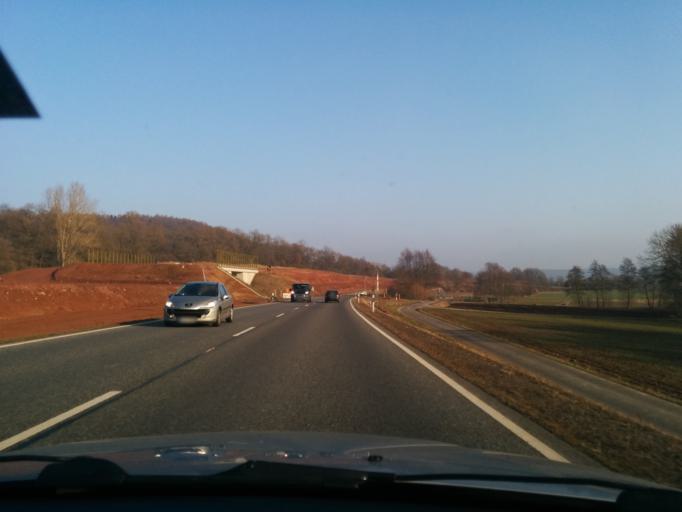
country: DE
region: Hesse
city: Waldkappel
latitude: 51.1509
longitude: 9.9087
